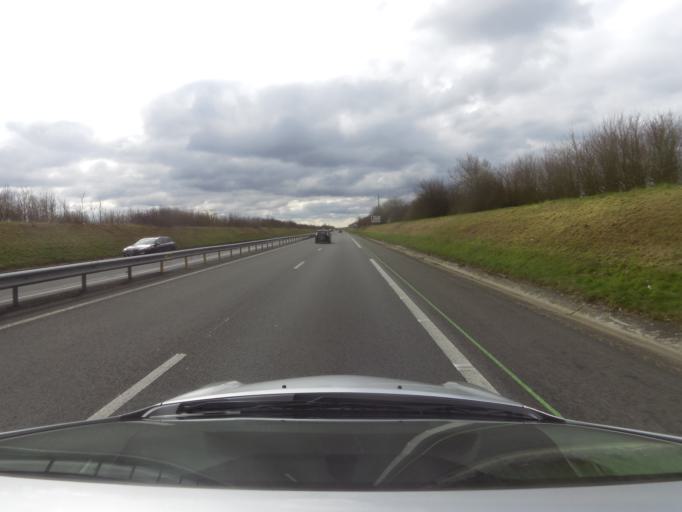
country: FR
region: Nord-Pas-de-Calais
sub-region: Departement du Pas-de-Calais
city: Etaples
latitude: 50.5313
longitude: 1.6827
